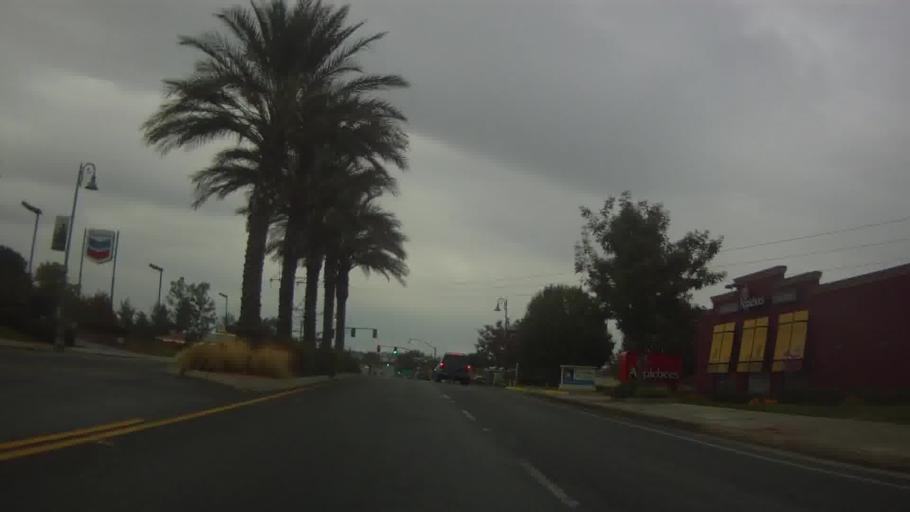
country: US
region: California
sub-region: Shasta County
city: Redding
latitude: 40.5809
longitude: -122.3578
